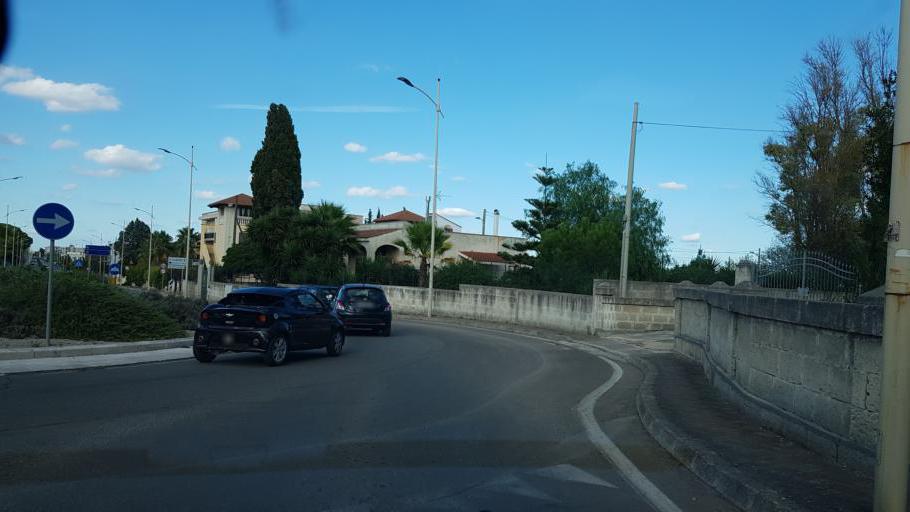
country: IT
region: Apulia
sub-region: Provincia di Lecce
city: Nardo
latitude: 40.1562
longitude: 18.0193
